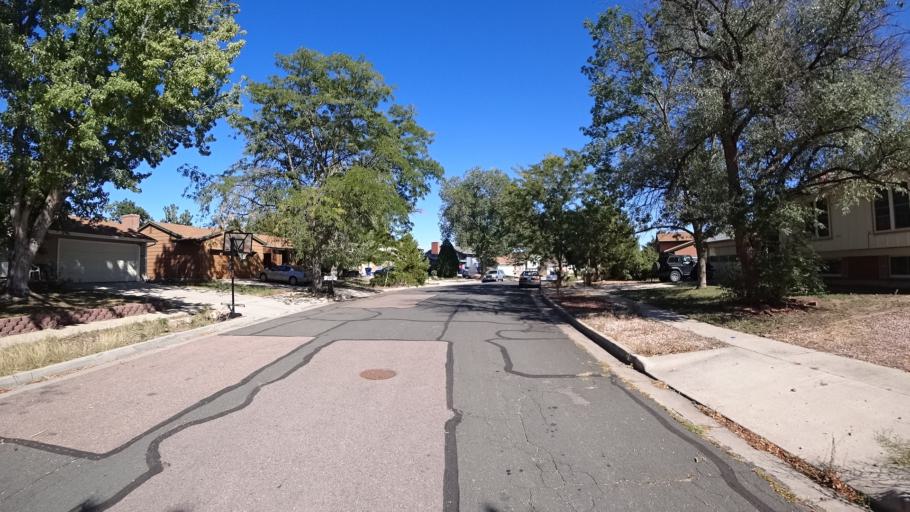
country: US
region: Colorado
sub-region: El Paso County
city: Stratmoor
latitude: 38.7915
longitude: -104.7444
